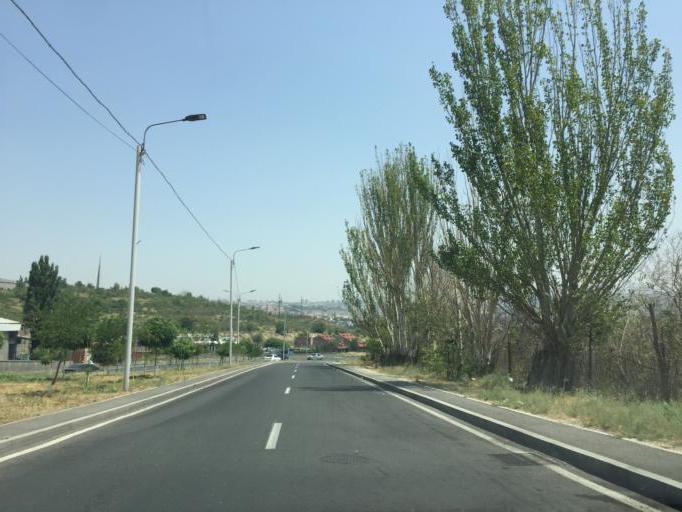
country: AM
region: Yerevan
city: Yerevan
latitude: 40.1812
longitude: 44.4844
